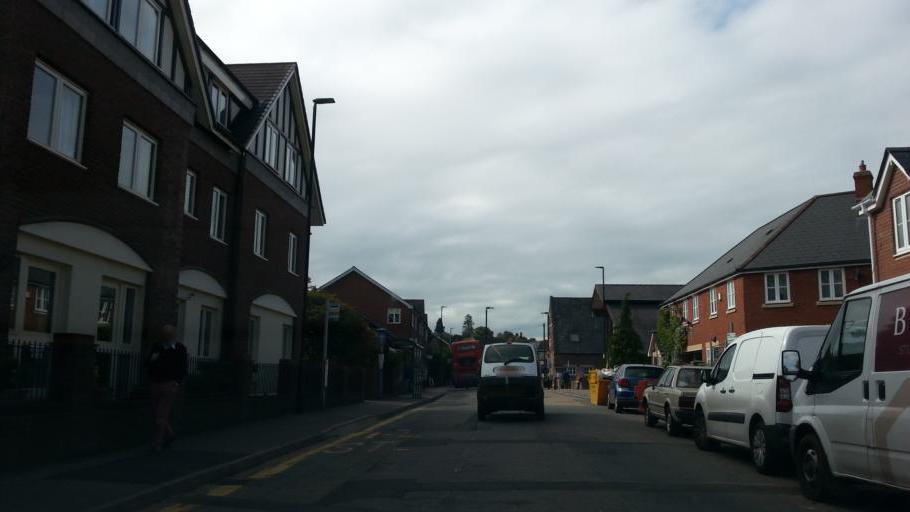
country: GB
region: England
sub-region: Herefordshire
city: Ross on Wye
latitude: 51.9149
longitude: -2.5798
